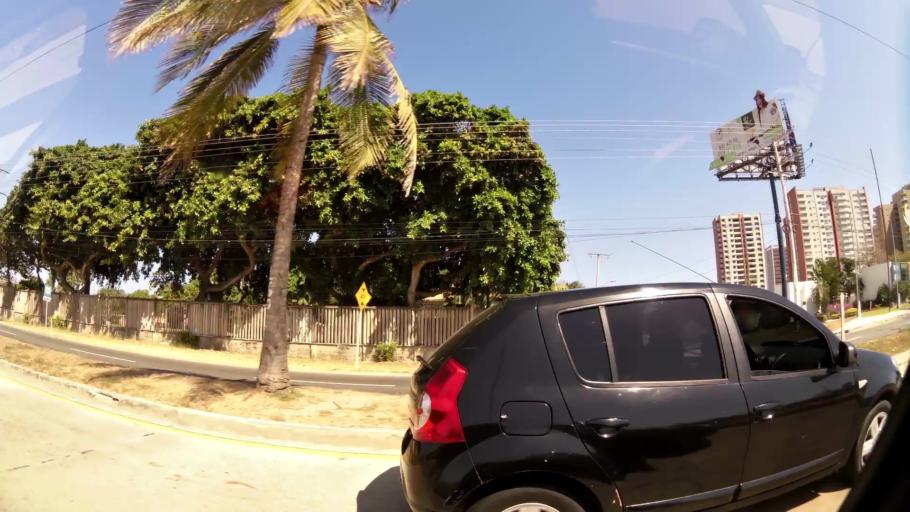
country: CO
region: Atlantico
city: Barranquilla
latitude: 11.0158
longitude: -74.8424
